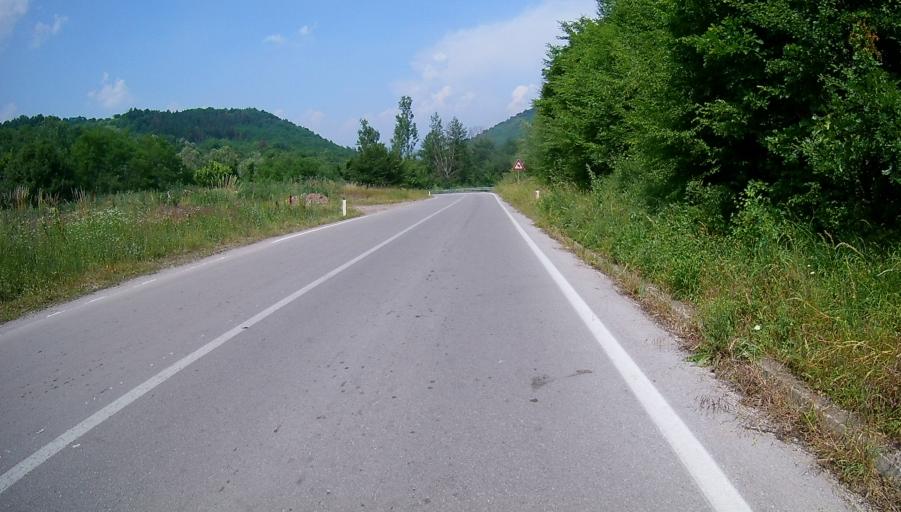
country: RS
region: Central Serbia
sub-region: Nisavski Okrug
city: Gadzin Han
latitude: 43.1883
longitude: 22.0202
